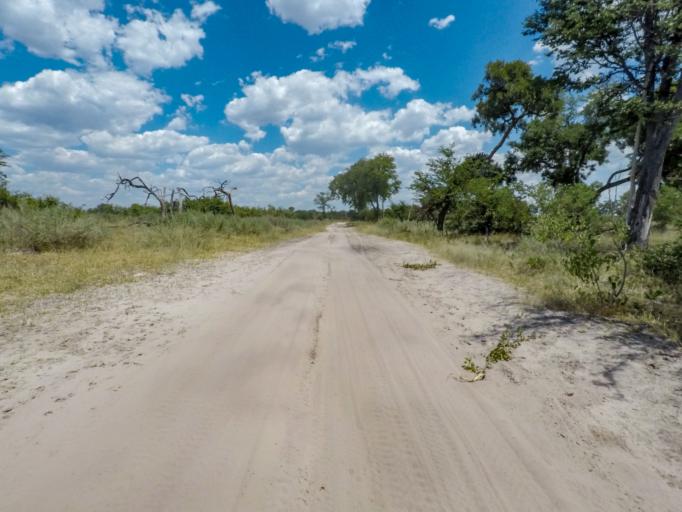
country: BW
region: North West
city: Maun
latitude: -19.1755
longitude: 23.7509
